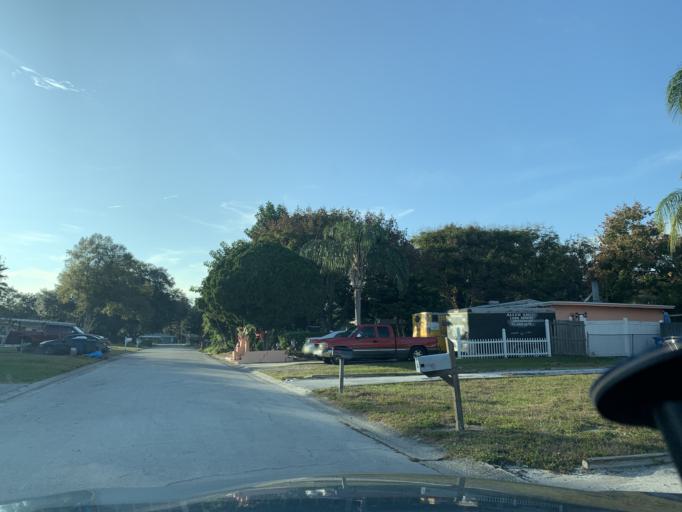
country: US
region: Florida
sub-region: Pinellas County
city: Ridgecrest
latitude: 27.8779
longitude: -82.7957
